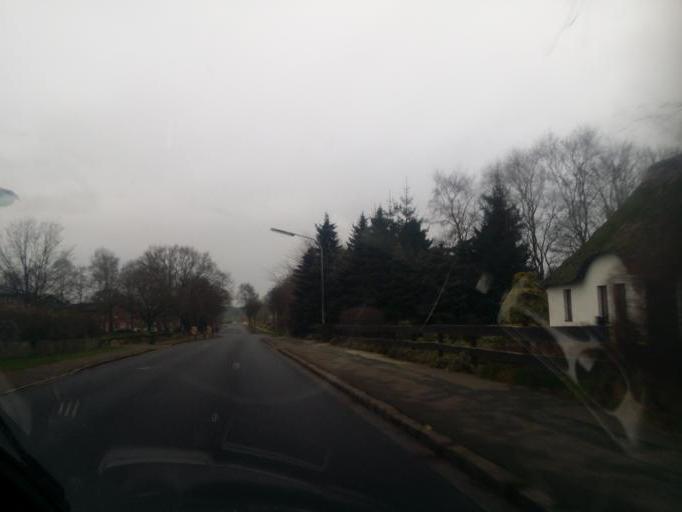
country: DE
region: Schleswig-Holstein
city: Suderheistedt
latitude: 54.2319
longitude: 9.1432
